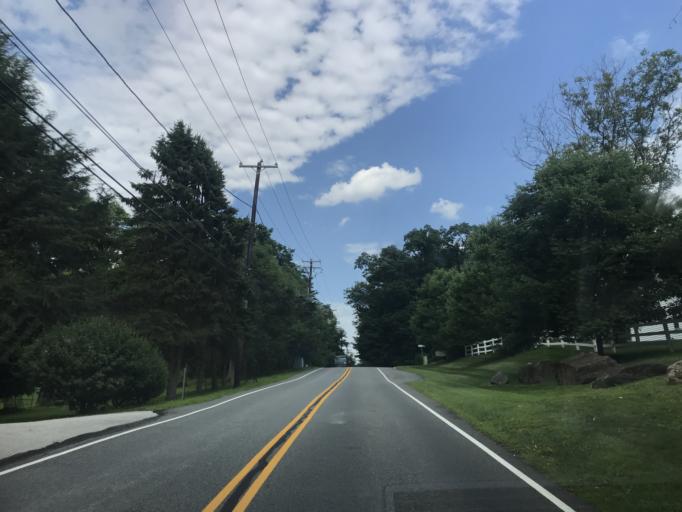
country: US
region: Pennsylvania
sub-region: Delaware County
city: Chester Heights
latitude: 39.8549
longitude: -75.5458
